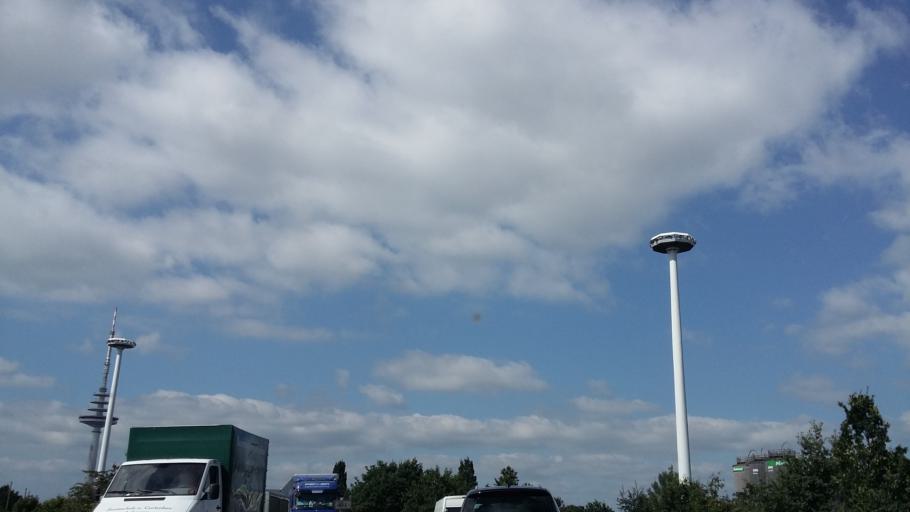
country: DE
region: Bremen
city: Bremen
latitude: 53.0874
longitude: 8.7975
